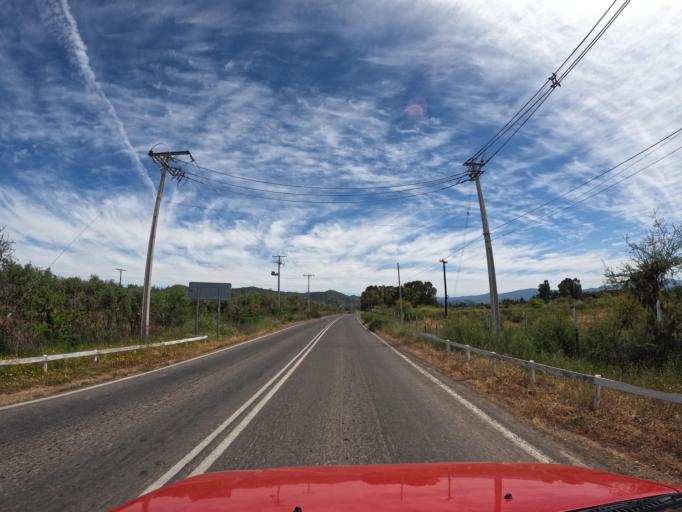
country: CL
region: Maule
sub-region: Provincia de Talca
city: Talca
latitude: -35.1108
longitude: -71.6299
